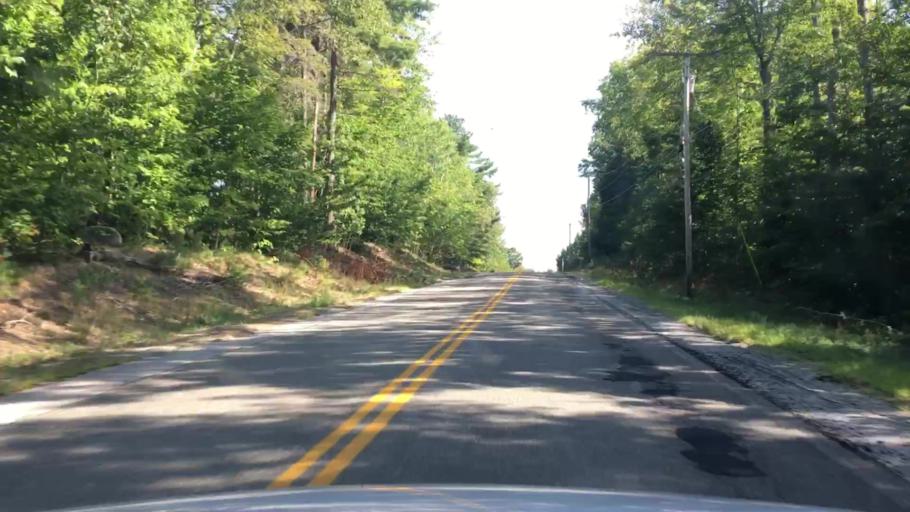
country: US
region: Maine
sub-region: Penobscot County
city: Enfield
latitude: 45.2116
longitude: -68.5245
